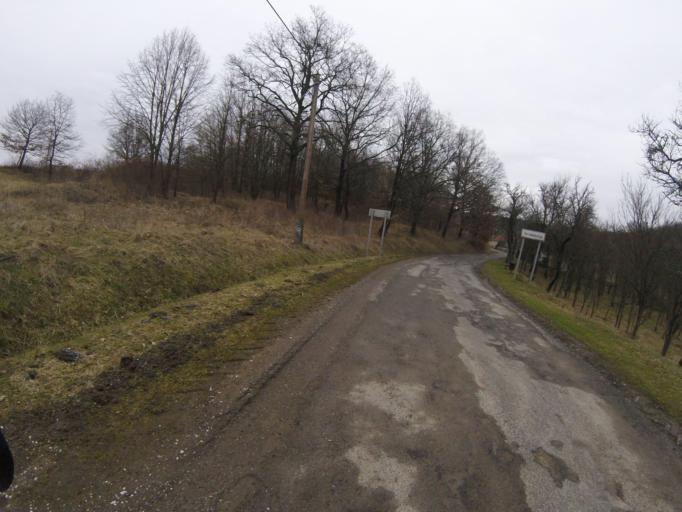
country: HU
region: Borsod-Abauj-Zemplen
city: Rudabanya
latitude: 48.4640
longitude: 20.6135
